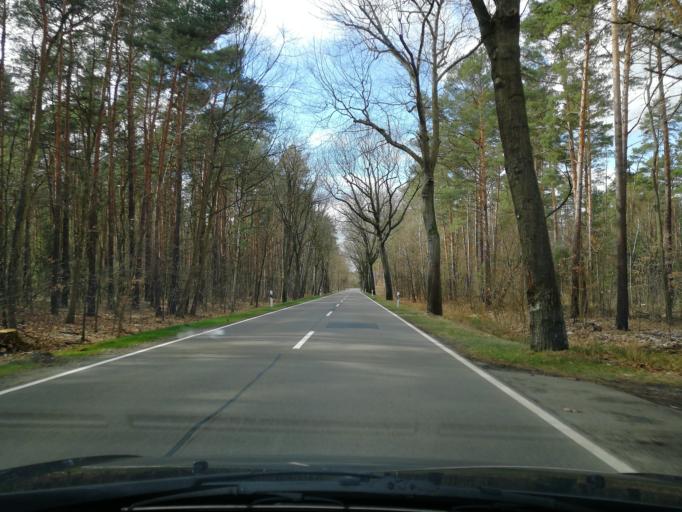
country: DE
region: Brandenburg
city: Altdobern
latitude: 51.7150
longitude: 14.0254
